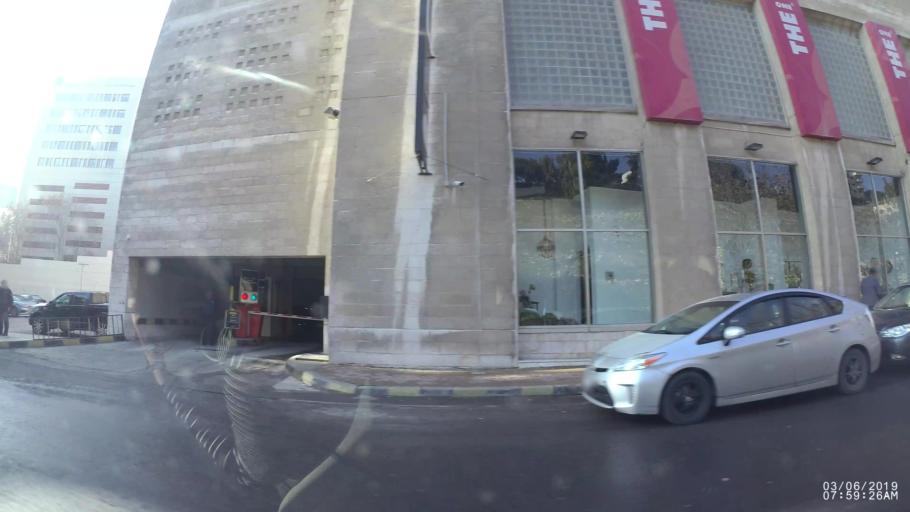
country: JO
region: Amman
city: Amman
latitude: 31.9572
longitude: 35.9105
